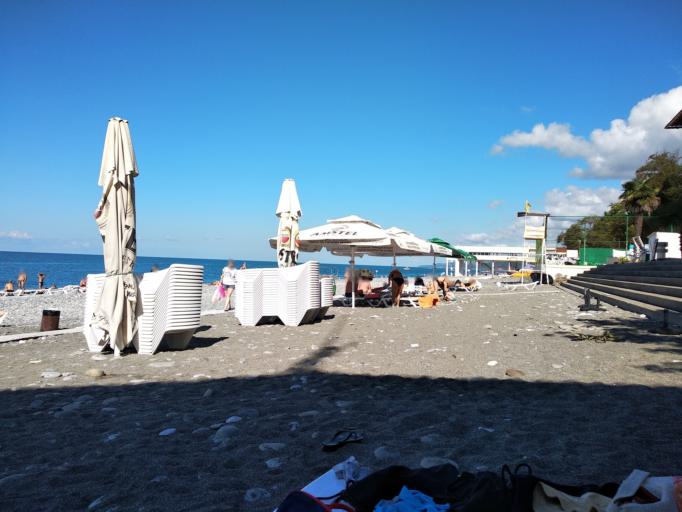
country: RU
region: Krasnodarskiy
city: Gornoye Loo
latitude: 43.6701
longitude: 39.6058
